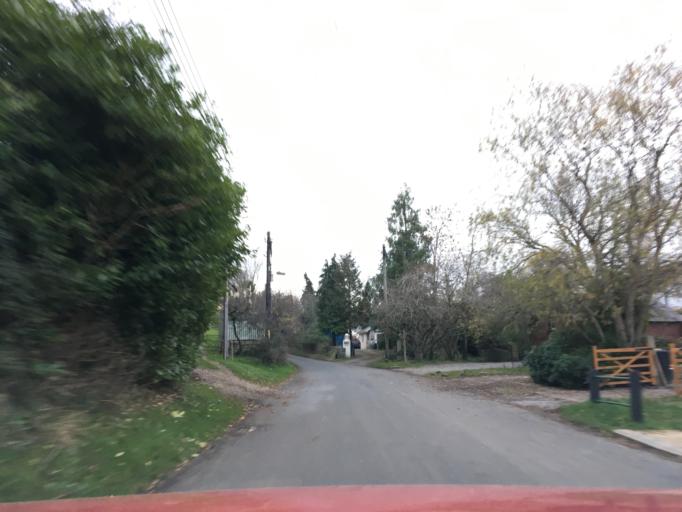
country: GB
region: Wales
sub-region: Newport
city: Bishton
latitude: 51.5852
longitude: -2.8783
